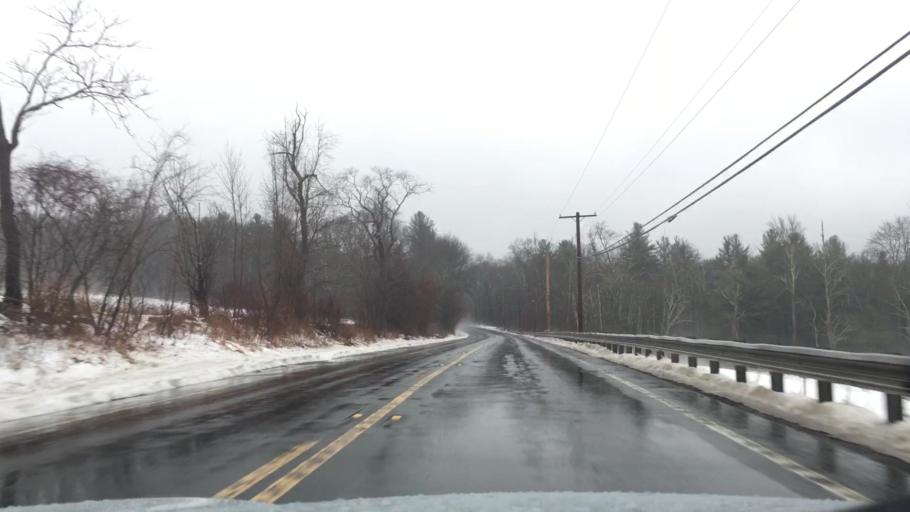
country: US
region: Massachusetts
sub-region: Hampshire County
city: Belchertown
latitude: 42.3133
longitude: -72.4063
